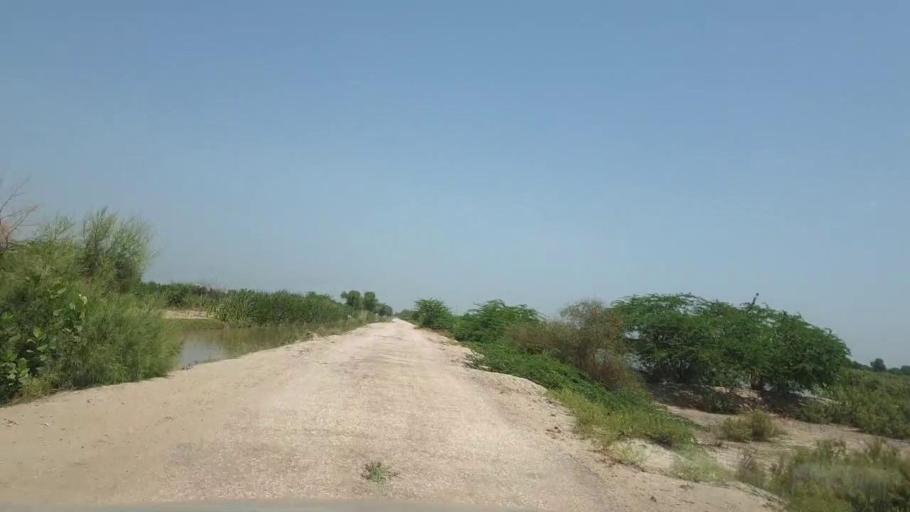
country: PK
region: Sindh
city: Rohri
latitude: 27.6381
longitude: 69.1019
